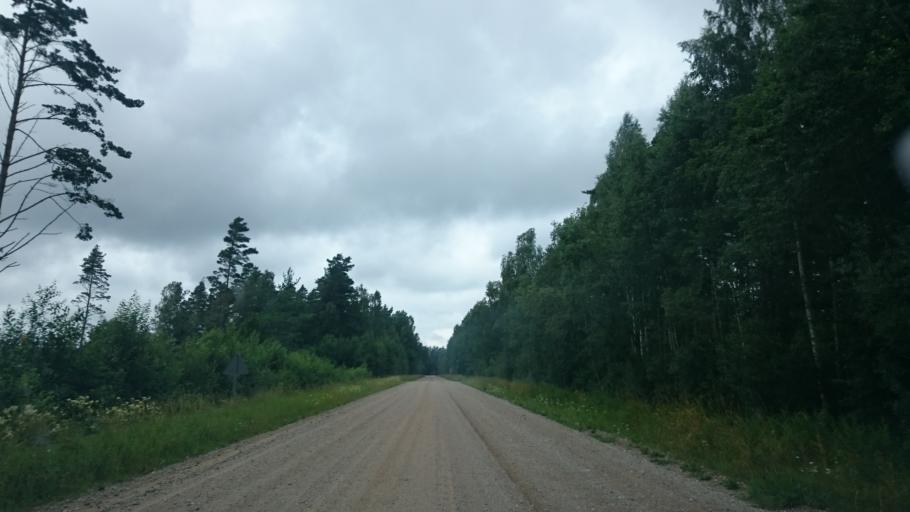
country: LV
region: Pavilostas
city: Pavilosta
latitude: 56.8587
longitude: 21.2277
